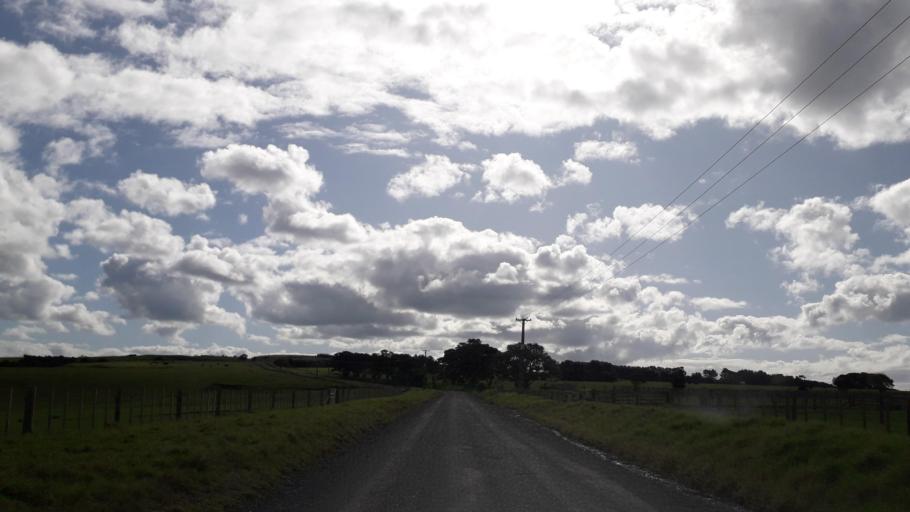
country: NZ
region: Northland
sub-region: Far North District
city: Kerikeri
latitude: -35.1377
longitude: 174.0322
